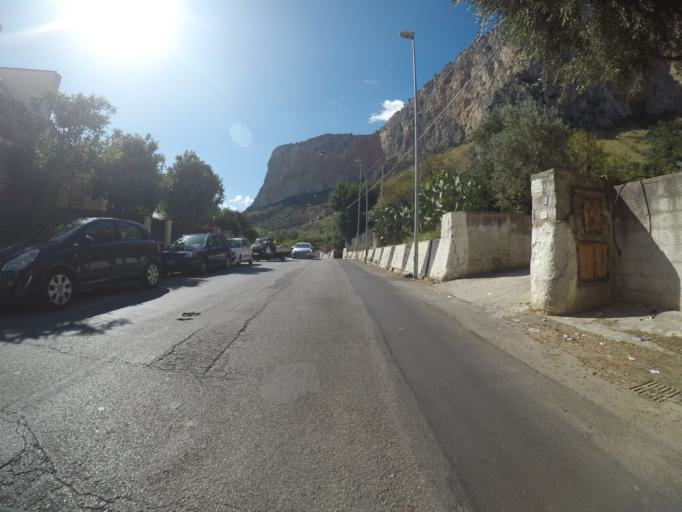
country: IT
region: Sicily
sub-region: Palermo
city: Palermo
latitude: 38.1661
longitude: 13.3658
